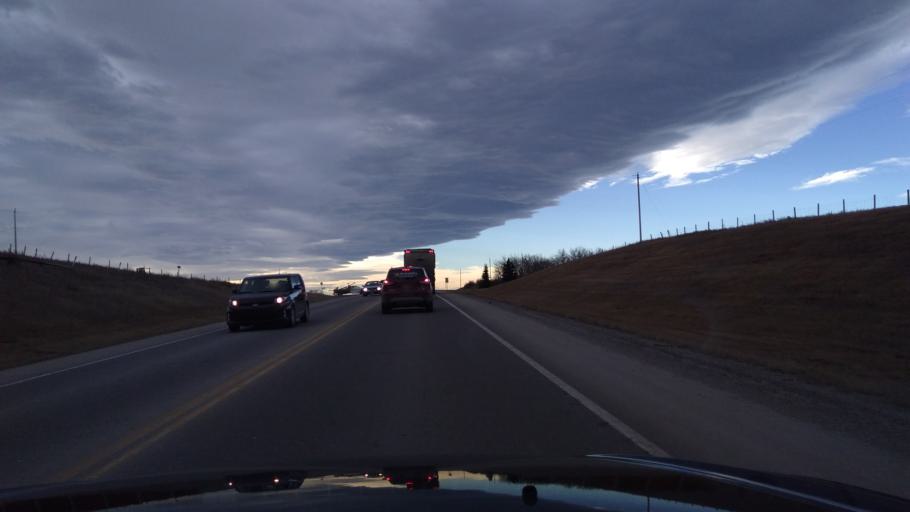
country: CA
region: Alberta
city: Cochrane
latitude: 51.1447
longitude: -114.4667
